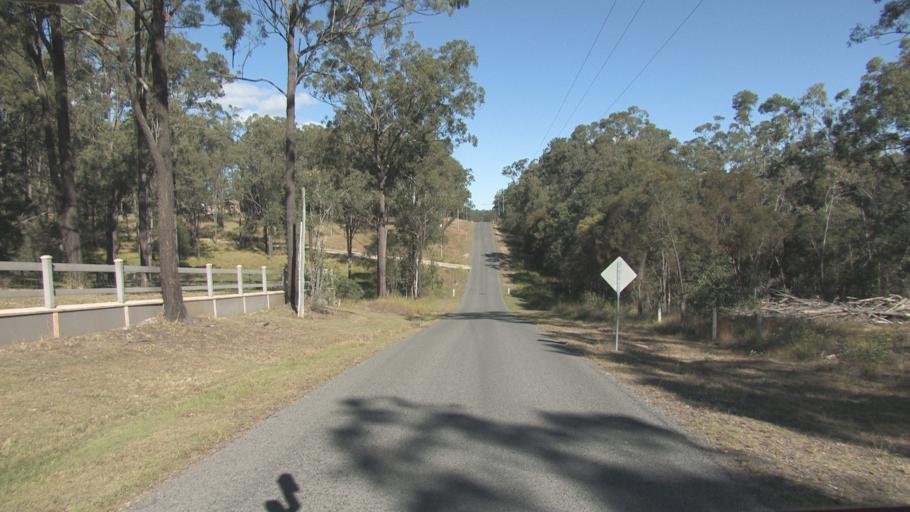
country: AU
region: Queensland
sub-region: Logan
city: Chambers Flat
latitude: -27.8131
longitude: 153.0779
